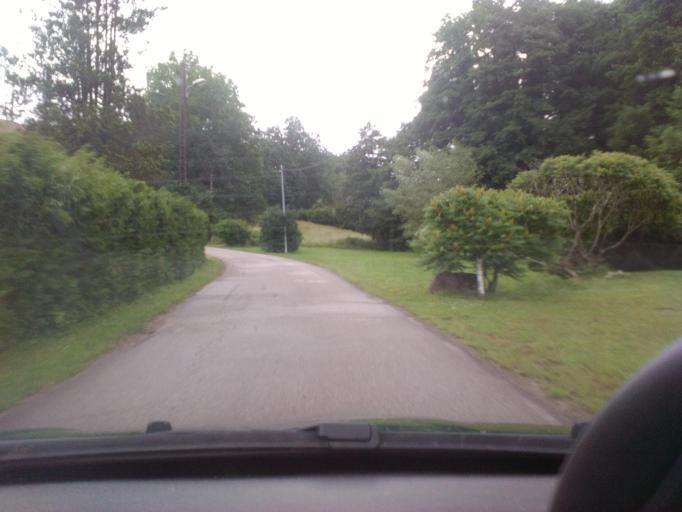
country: FR
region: Lorraine
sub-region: Departement des Vosges
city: Saint-Michel-sur-Meurthe
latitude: 48.3286
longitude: 6.9176
